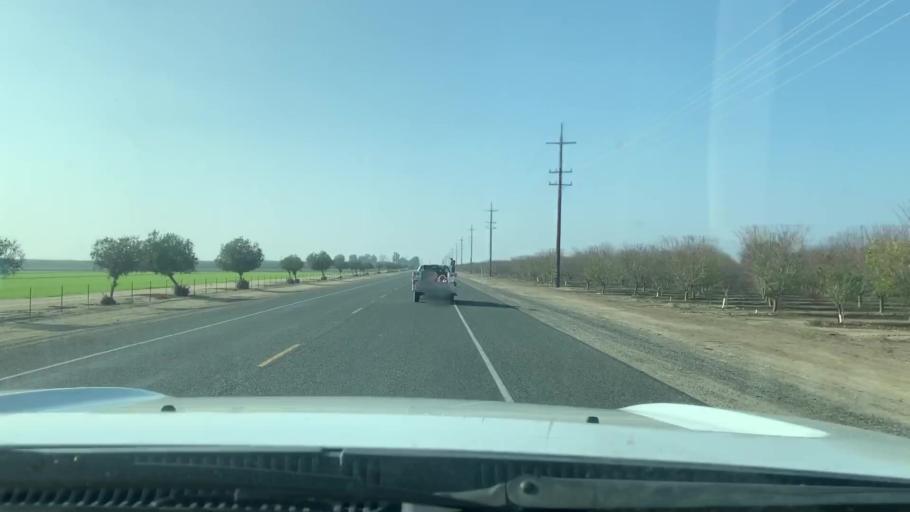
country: US
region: California
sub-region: Kern County
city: Wasco
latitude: 35.6015
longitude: -119.4129
